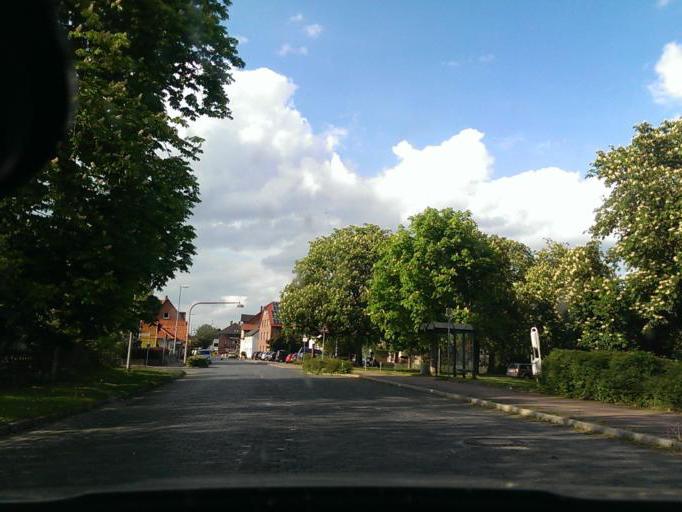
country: DE
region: Lower Saxony
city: Banteln
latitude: 52.0660
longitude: 9.7527
